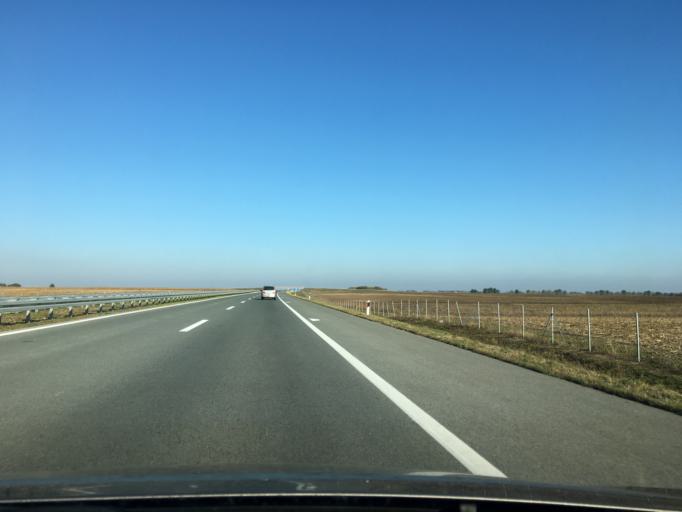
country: RS
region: Autonomna Pokrajina Vojvodina
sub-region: Severnobacki Okrug
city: Mali Igos
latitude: 45.7389
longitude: 19.7035
